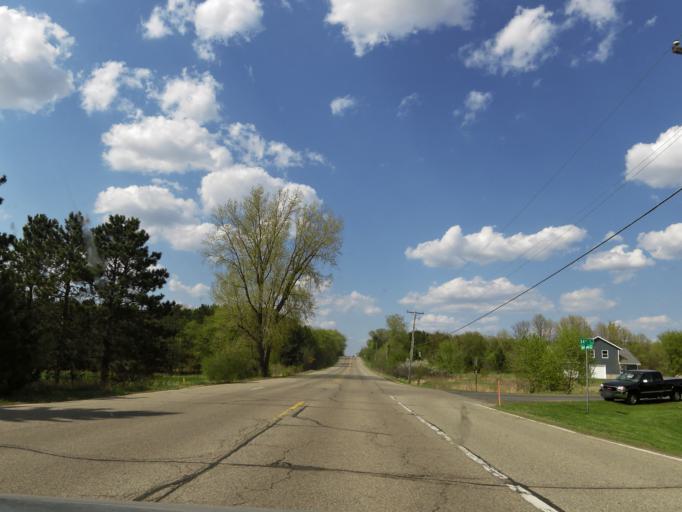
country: US
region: Minnesota
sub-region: Washington County
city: Oak Park Heights
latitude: 44.9986
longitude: -92.8225
